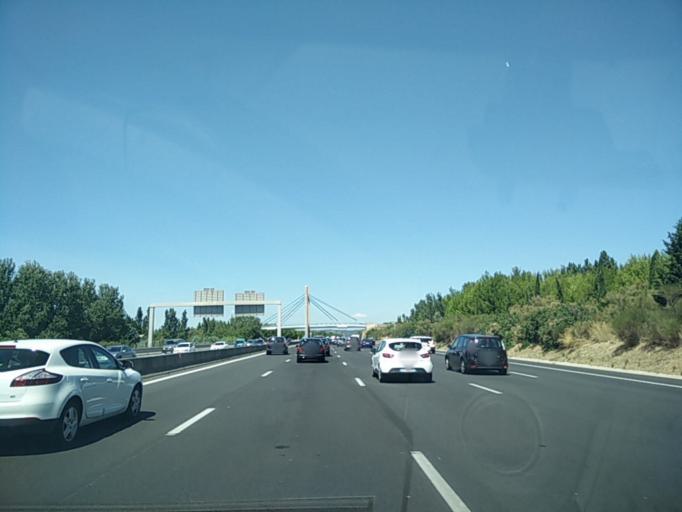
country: FR
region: Provence-Alpes-Cote d'Azur
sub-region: Departement du Vaucluse
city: Orange
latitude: 44.1422
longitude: 4.7782
